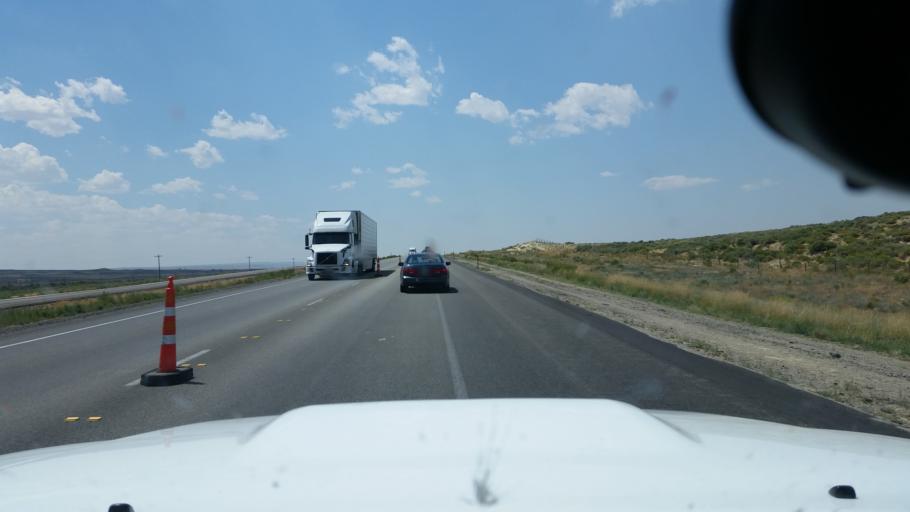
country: US
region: Wyoming
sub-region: Carbon County
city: Rawlins
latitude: 41.7004
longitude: -107.9117
